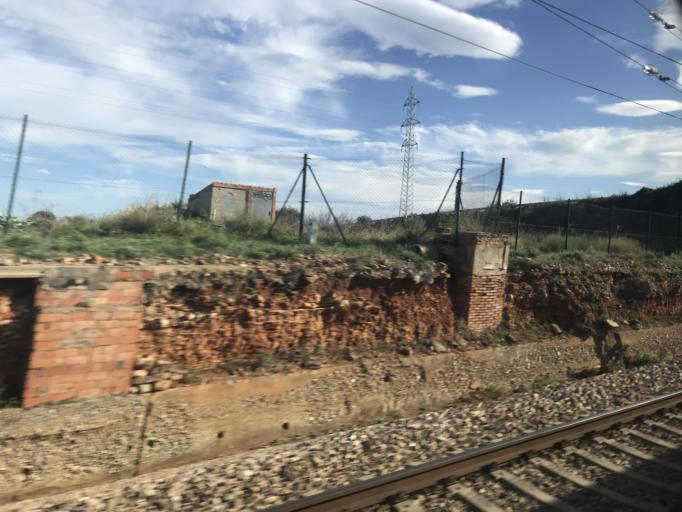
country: ES
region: Valencia
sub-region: Provincia de Castello
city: Torreblanca
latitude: 40.2246
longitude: 0.2120
